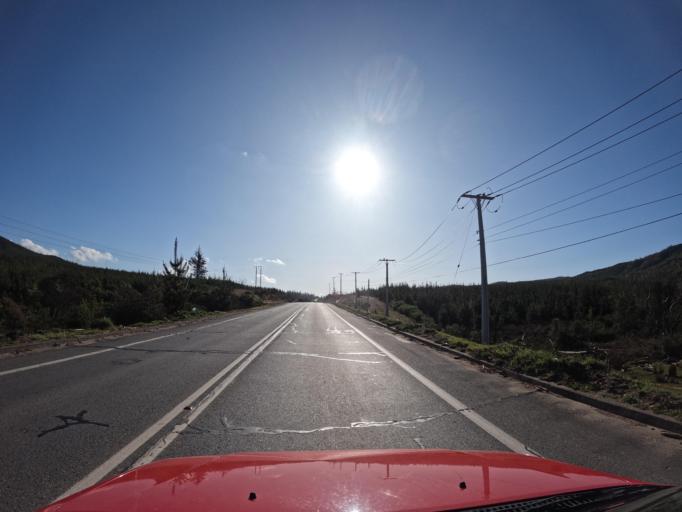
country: CL
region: Maule
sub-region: Provincia de Talca
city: Constitucion
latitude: -35.4459
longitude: -72.3158
